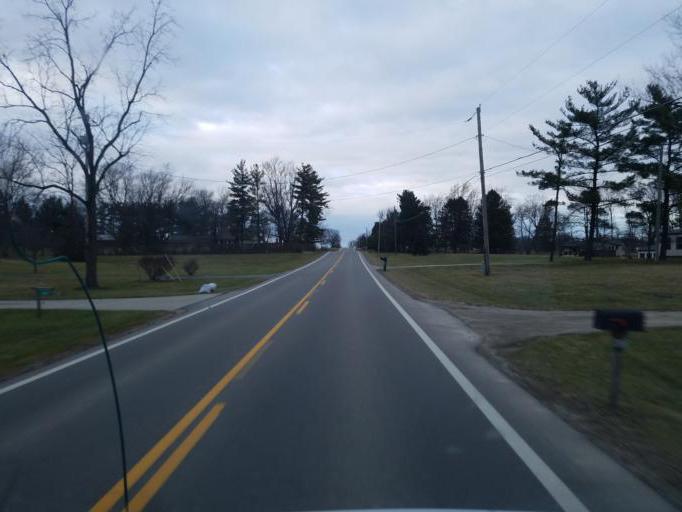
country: US
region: Ohio
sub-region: Delaware County
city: Delaware
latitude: 40.3274
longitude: -83.1300
